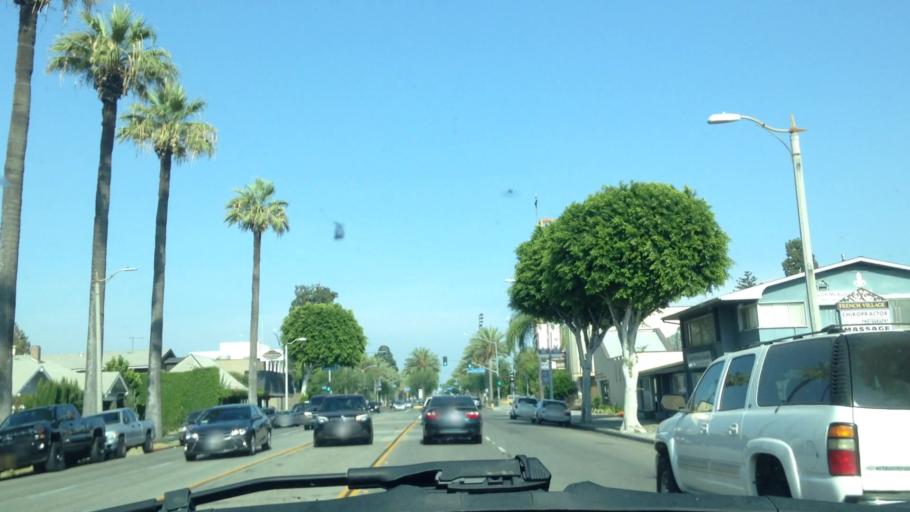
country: US
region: California
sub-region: Orange County
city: Fullerton
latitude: 33.8703
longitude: -117.9327
